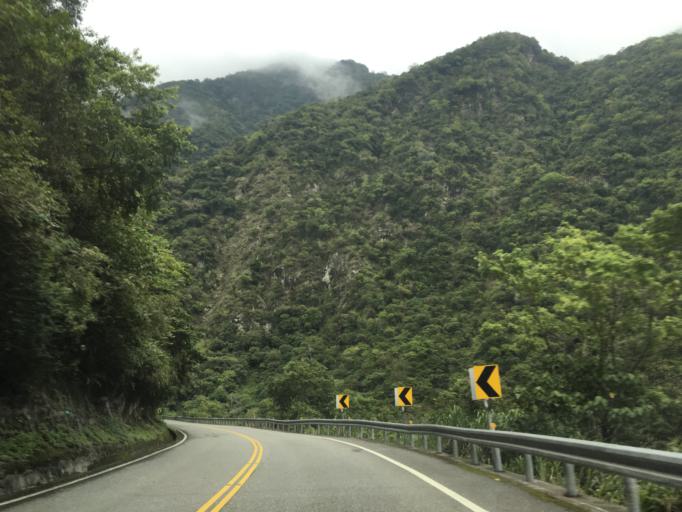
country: TW
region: Taiwan
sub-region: Hualien
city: Hualian
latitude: 24.1752
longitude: 121.5874
